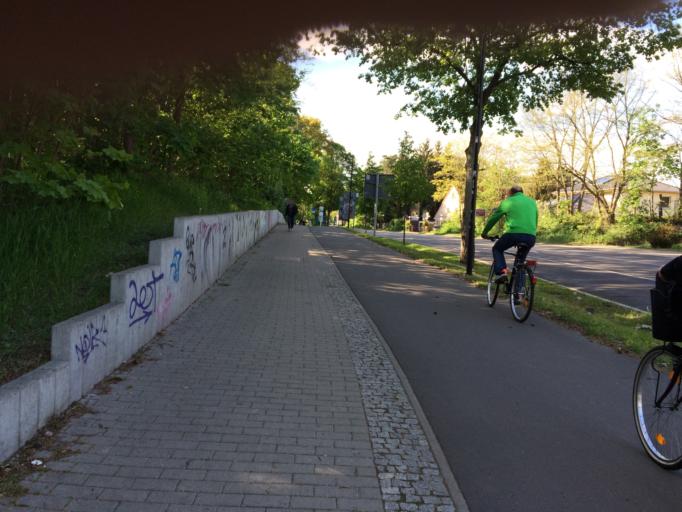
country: DE
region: Brandenburg
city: Potsdam
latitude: 52.3553
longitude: 13.1022
